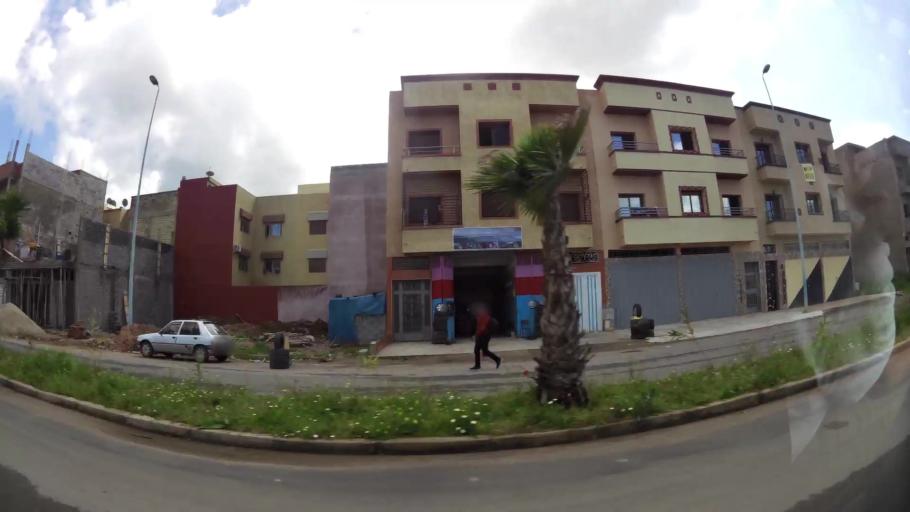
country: MA
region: Grand Casablanca
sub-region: Mediouna
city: Mediouna
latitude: 33.3898
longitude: -7.5329
